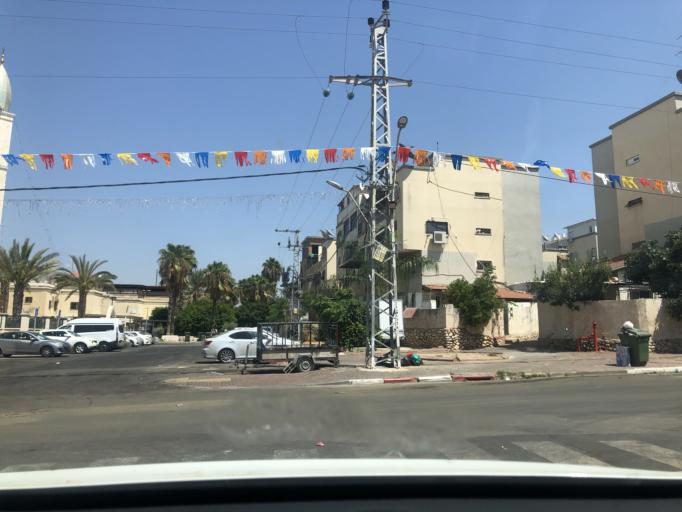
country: IL
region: Central District
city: Lod
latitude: 31.9575
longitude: 34.9020
